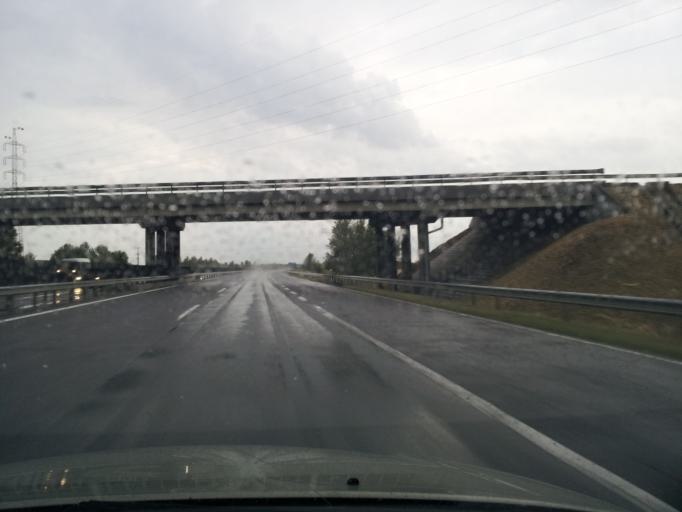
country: HU
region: Borsod-Abauj-Zemplen
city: Onod
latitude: 47.9801
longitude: 20.8978
